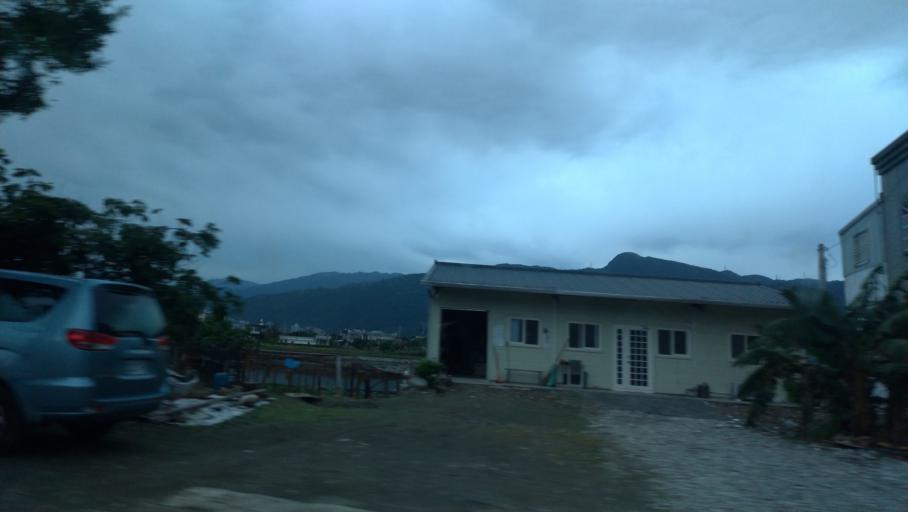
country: TW
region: Taiwan
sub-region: Yilan
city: Yilan
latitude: 24.8339
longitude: 121.8033
